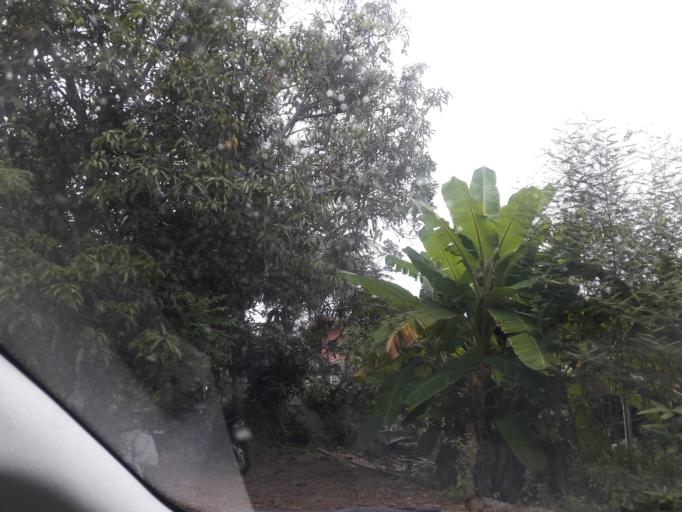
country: TH
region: Ratchaburi
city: Damnoen Saduak
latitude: 13.5350
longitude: 99.9349
